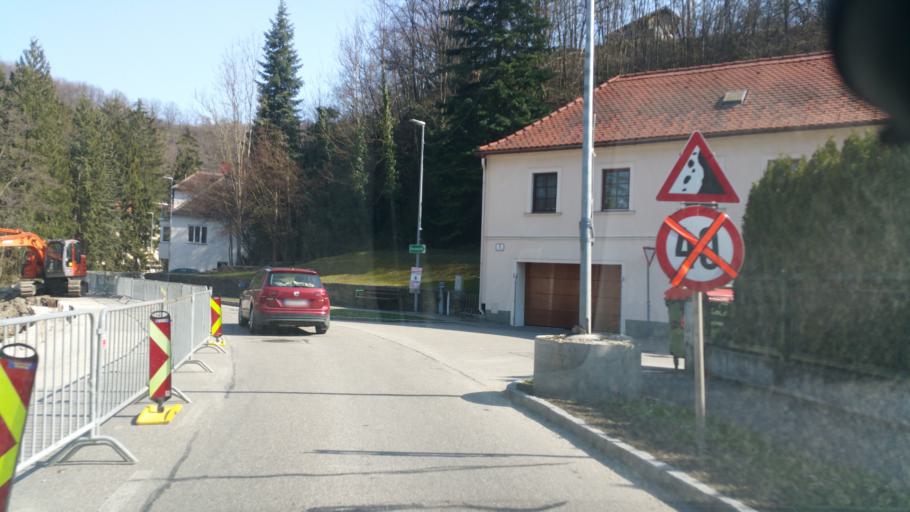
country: AT
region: Lower Austria
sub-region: Politischer Bezirk Krems
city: Stratzing
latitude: 48.4297
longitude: 15.5890
